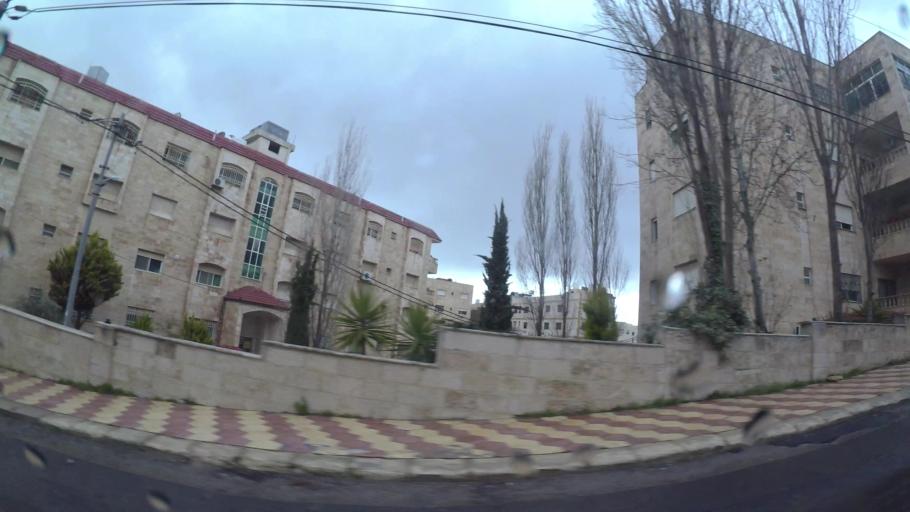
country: JO
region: Amman
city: Al Jubayhah
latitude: 32.0332
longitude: 35.8710
